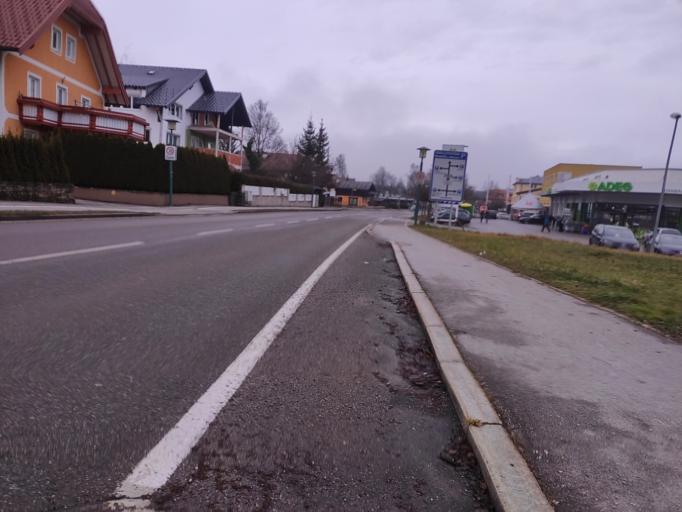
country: AT
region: Salzburg
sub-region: Politischer Bezirk Salzburg-Umgebung
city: Neumarkt am Wallersee
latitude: 47.9401
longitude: 13.2236
